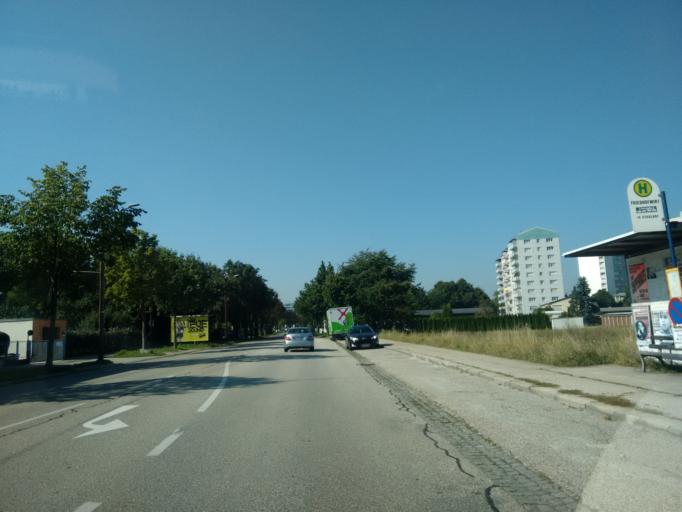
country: AT
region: Upper Austria
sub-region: Wels Stadt
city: Wels
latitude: 48.1697
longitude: 14.0330
